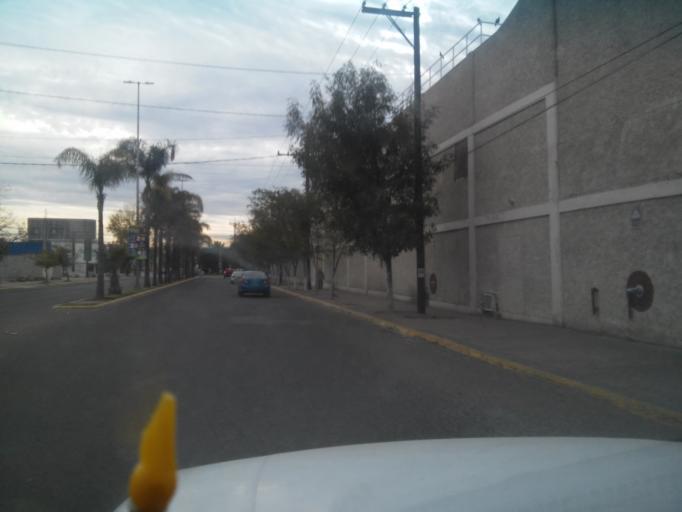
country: MX
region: Durango
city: Victoria de Durango
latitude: 24.0093
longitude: -104.6644
